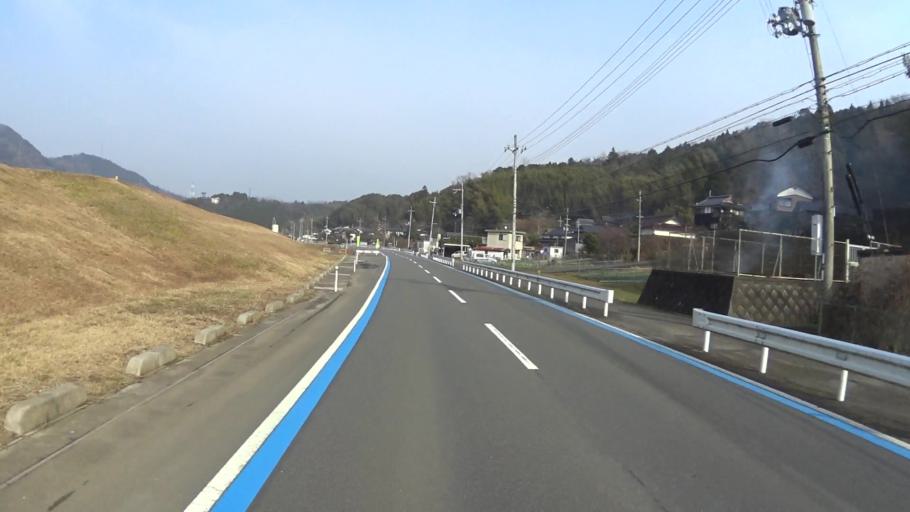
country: JP
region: Kyoto
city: Fukuchiyama
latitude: 35.3348
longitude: 135.1163
